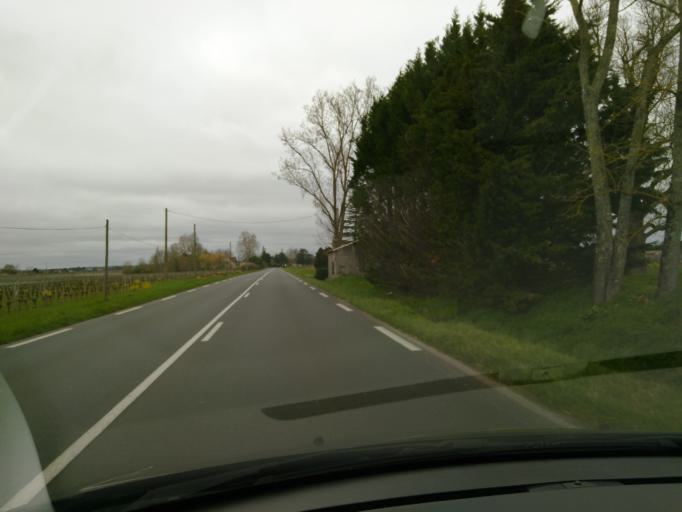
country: FR
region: Aquitaine
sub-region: Departement de la Dordogne
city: Monbazillac
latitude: 44.8108
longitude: 0.5097
